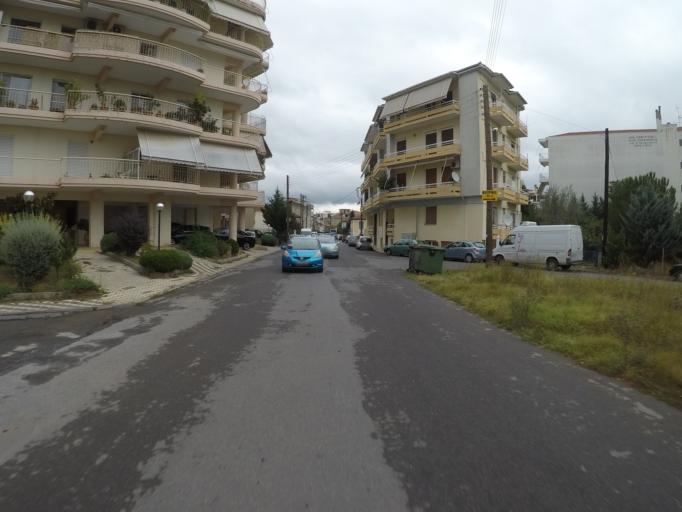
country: GR
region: Peloponnese
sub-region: Nomos Arkadias
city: Tripoli
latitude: 37.5177
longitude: 22.3745
